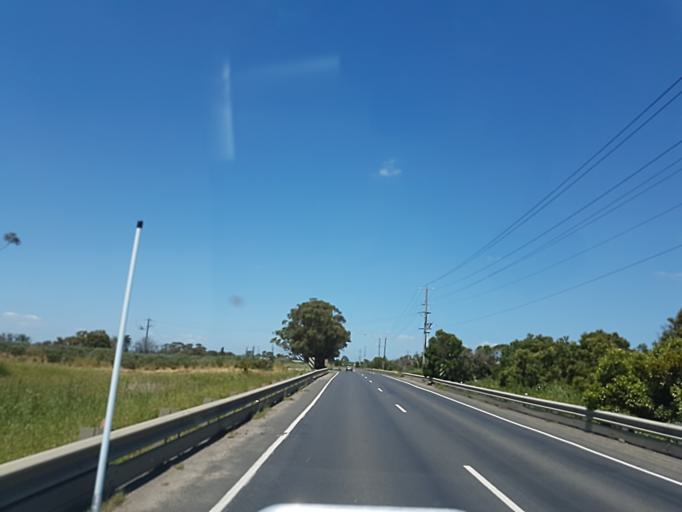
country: AU
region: Victoria
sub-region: Cardinia
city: Pakenham South
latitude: -38.1140
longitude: 145.4855
